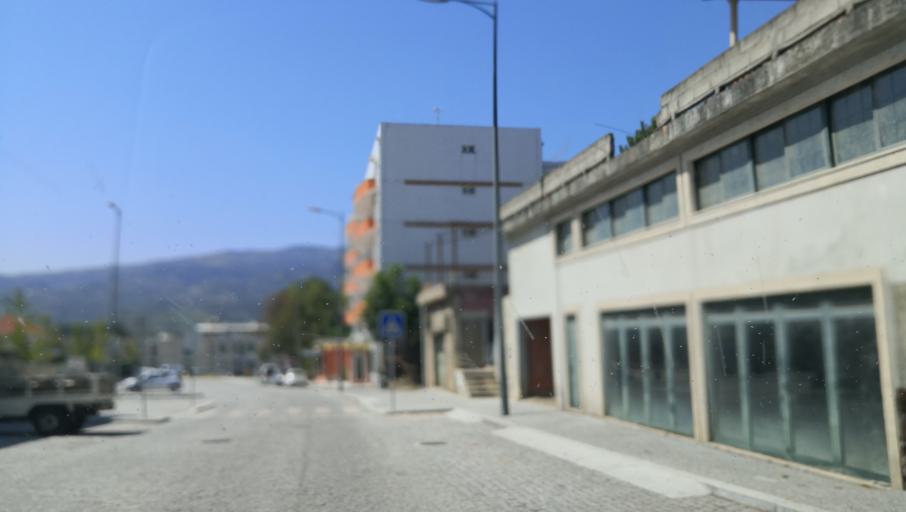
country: PT
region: Vila Real
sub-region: Peso da Regua
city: Peso da Regua
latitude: 41.1666
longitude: -7.7914
